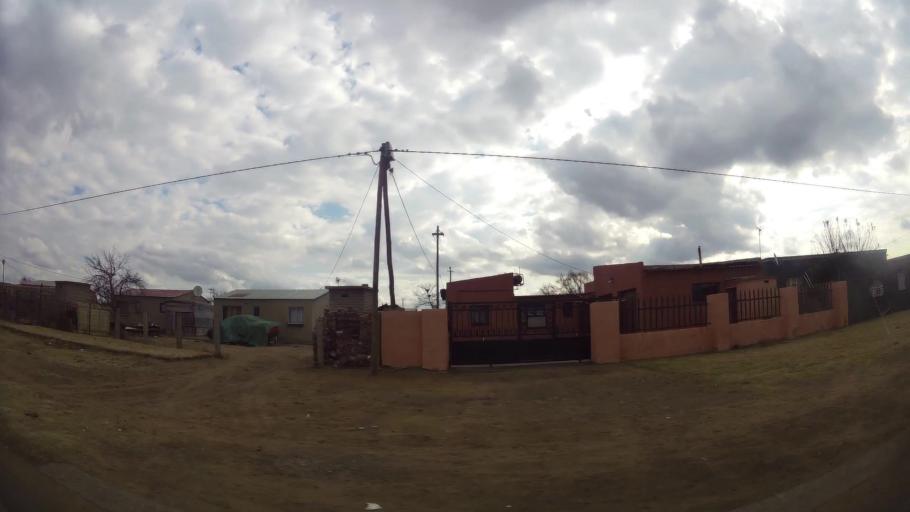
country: ZA
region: Orange Free State
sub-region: Fezile Dabi District Municipality
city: Sasolburg
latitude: -26.8606
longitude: 27.8527
